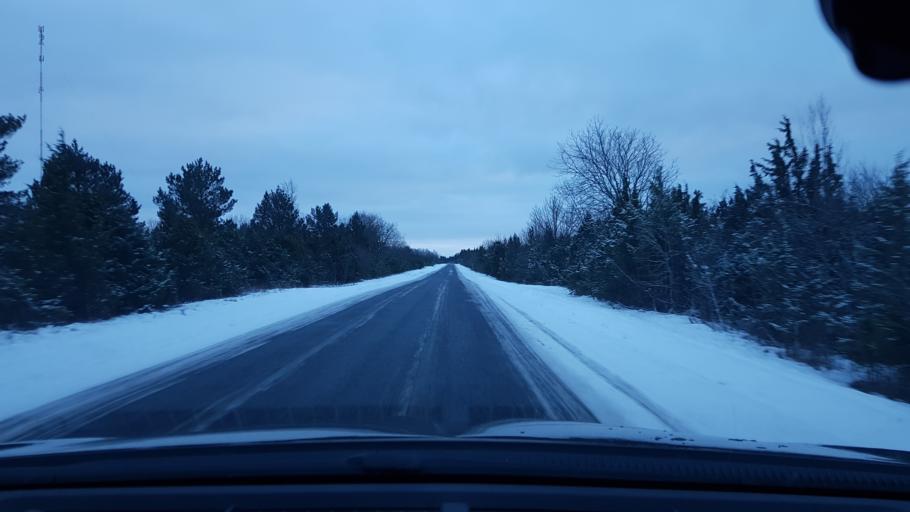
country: EE
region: Laeaene
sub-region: Haapsalu linn
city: Haapsalu
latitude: 59.1152
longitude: 23.5326
